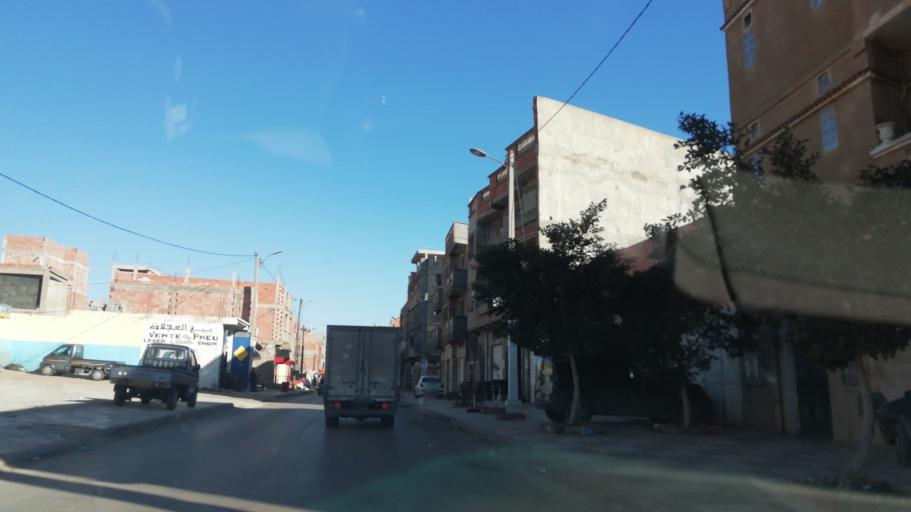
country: DZ
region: Oran
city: Bir el Djir
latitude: 35.7260
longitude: -0.5443
